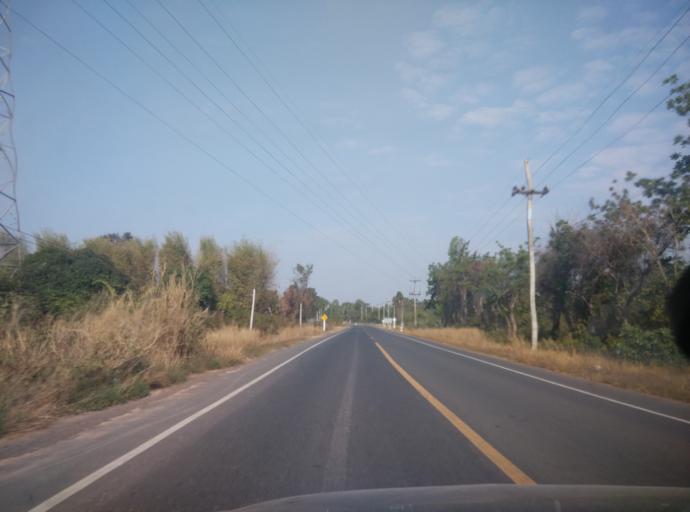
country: TH
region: Sisaket
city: Si Sa Ket
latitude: 15.1125
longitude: 104.2690
